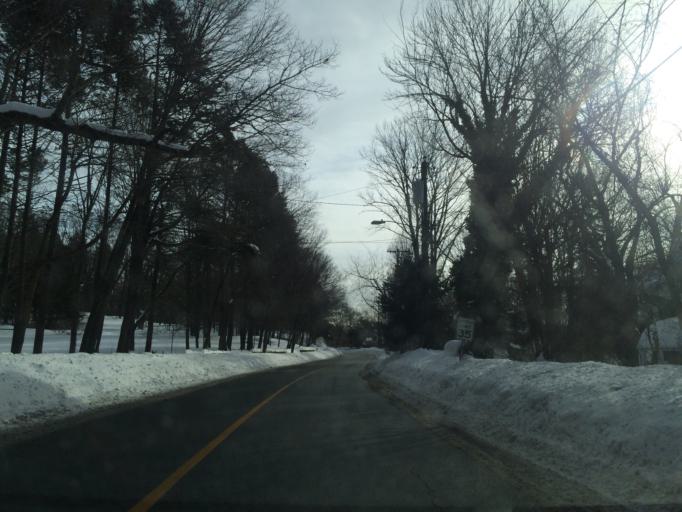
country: US
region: Massachusetts
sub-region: Middlesex County
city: Weston
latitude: 42.3681
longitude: -71.2957
